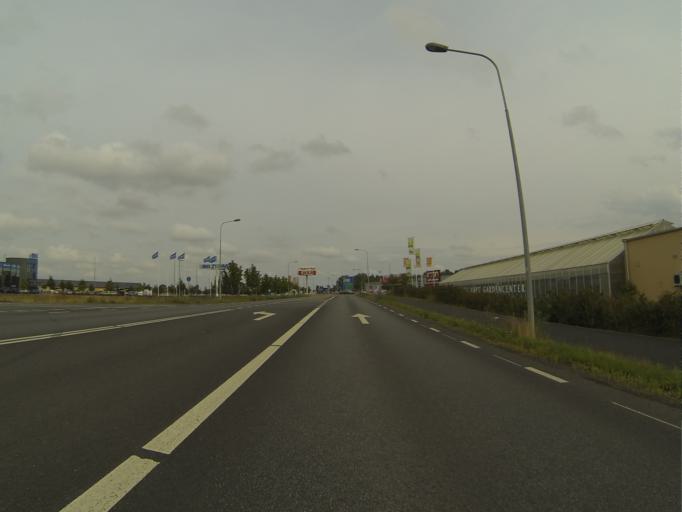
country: SE
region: Skane
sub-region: Kristianstads Kommun
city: Kristianstad
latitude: 56.0222
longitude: 14.1115
